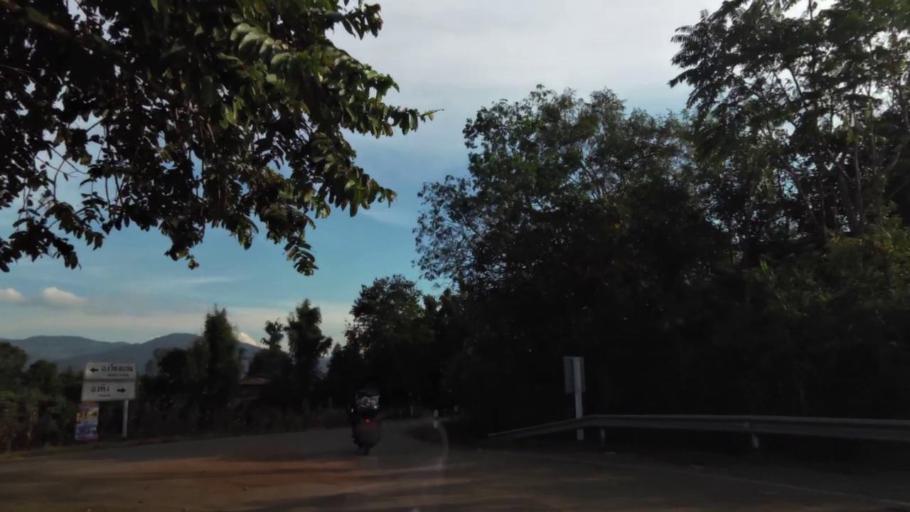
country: TH
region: Chiang Rai
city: Khun Tan
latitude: 19.8605
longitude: 100.3677
